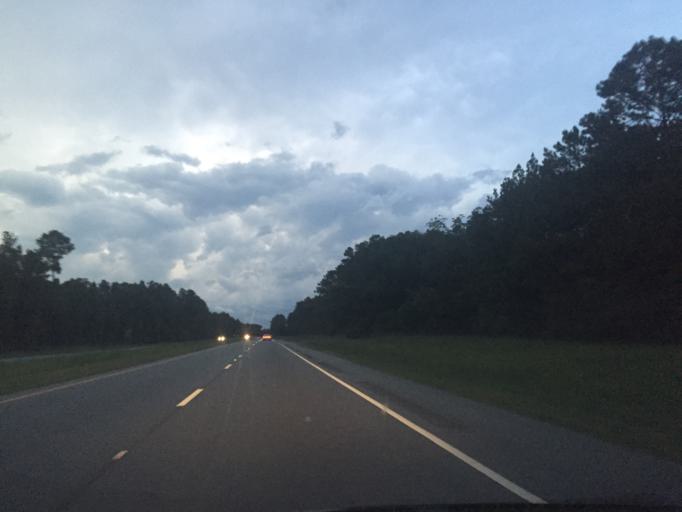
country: US
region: Georgia
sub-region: Liberty County
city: Midway
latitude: 31.8424
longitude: -81.4757
